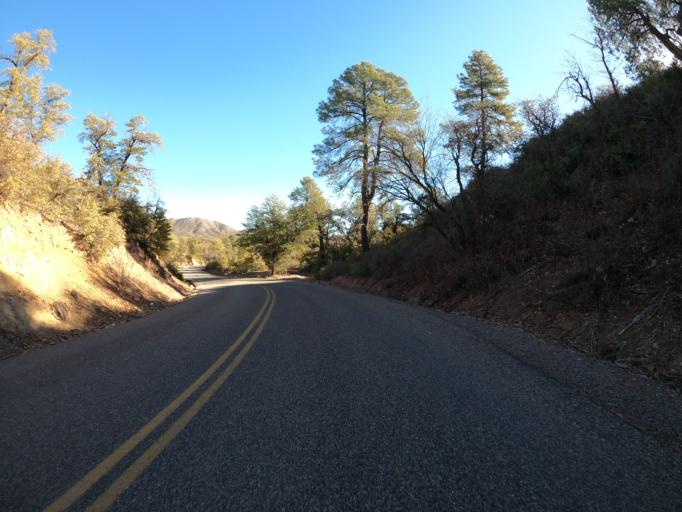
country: US
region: Arizona
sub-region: Yavapai County
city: Verde Village
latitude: 34.5876
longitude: -112.0555
